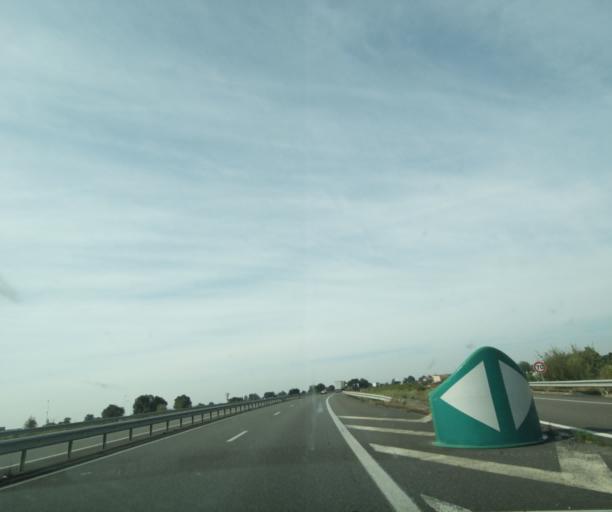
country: FR
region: Bourgogne
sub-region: Departement de Saone-et-Loire
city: Paray-le-Monial
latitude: 46.4647
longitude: 4.0848
